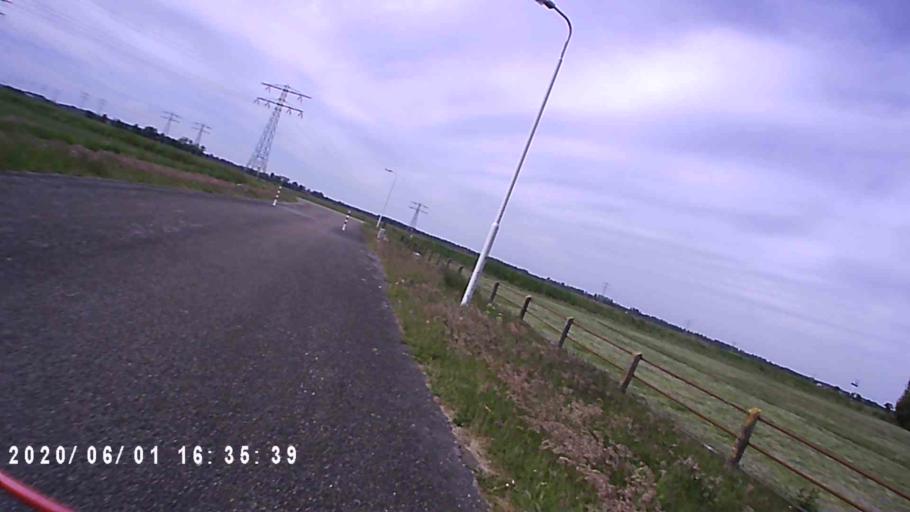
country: NL
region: Friesland
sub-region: Gemeente Leeuwarden
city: Camminghaburen
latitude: 53.1926
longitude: 5.8762
